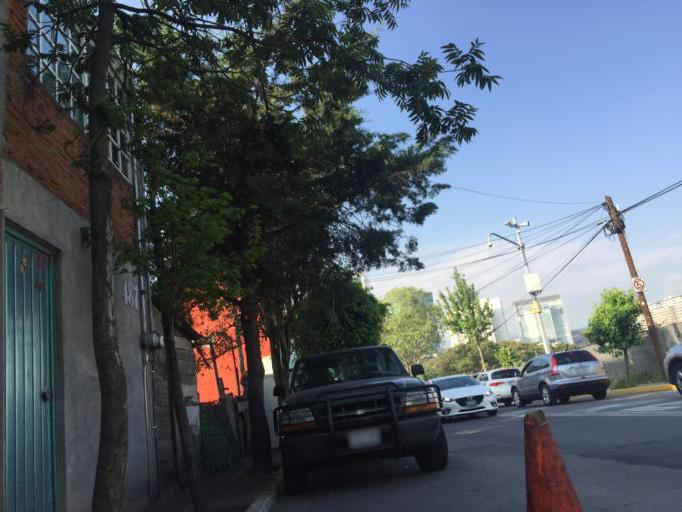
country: MX
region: Mexico City
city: Col. Bosques de las Lomas
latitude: 19.3885
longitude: -99.2653
